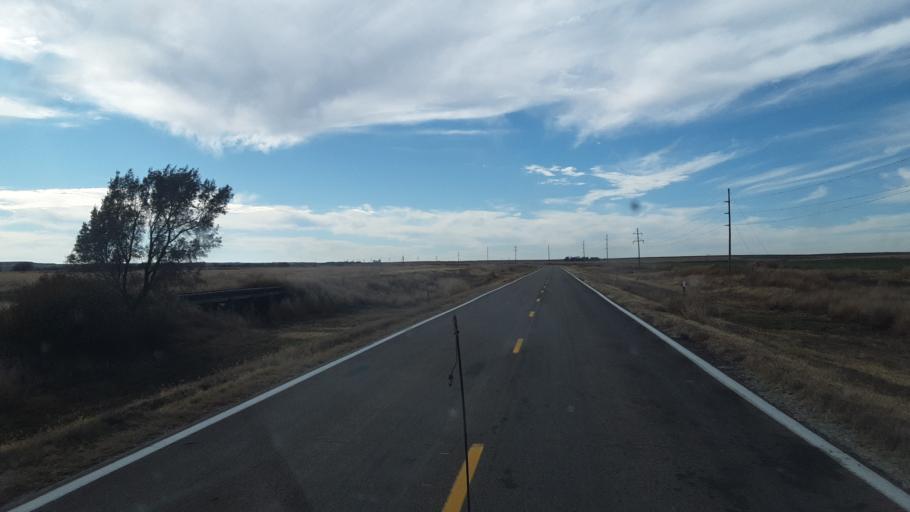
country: US
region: Kansas
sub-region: Hodgeman County
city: Jetmore
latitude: 38.0933
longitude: -99.8083
